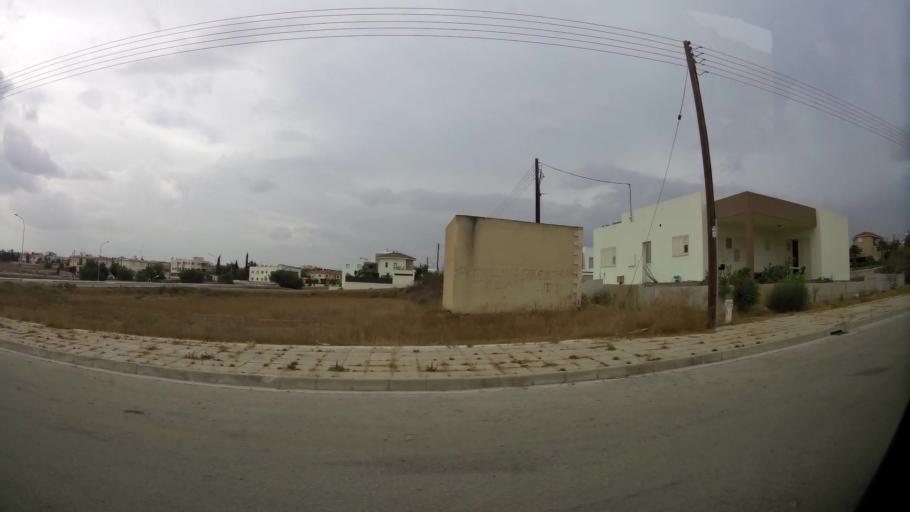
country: CY
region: Lefkosia
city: Geri
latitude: 35.0808
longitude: 33.3963
